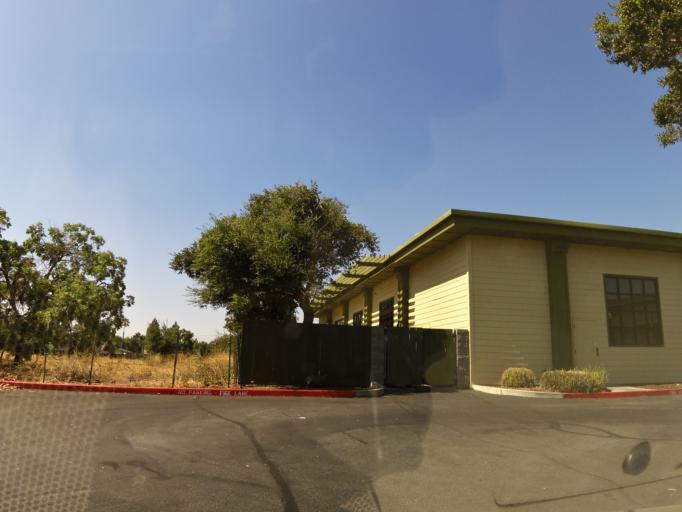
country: US
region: California
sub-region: Santa Clara County
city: Morgan Hill
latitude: 37.1301
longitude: -121.6393
